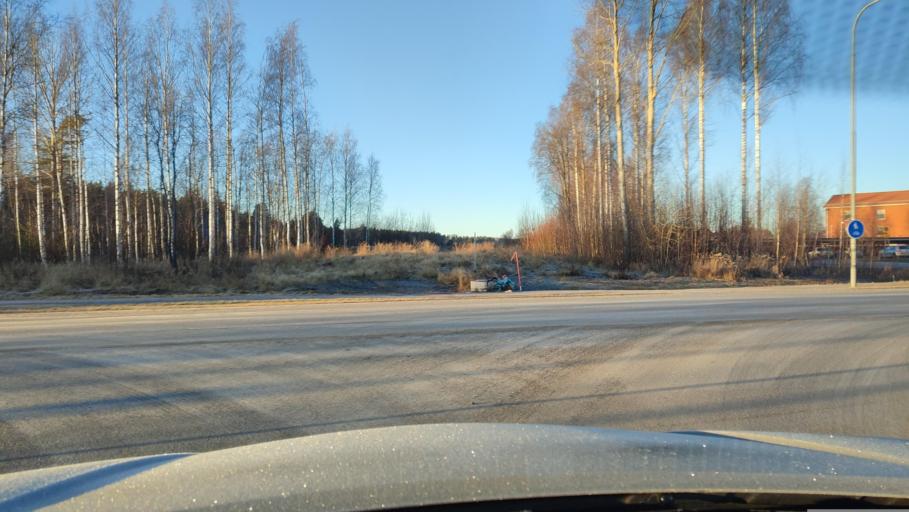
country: SE
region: Vaesterbotten
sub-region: Skelleftea Kommun
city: Skelleftea
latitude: 64.7406
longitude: 20.9425
